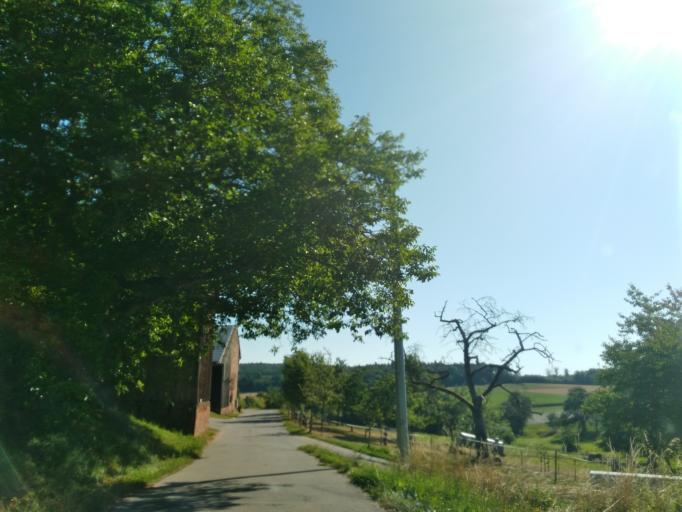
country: DE
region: Baden-Wuerttemberg
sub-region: Karlsruhe Region
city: Buchen
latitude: 49.5249
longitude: 9.2705
